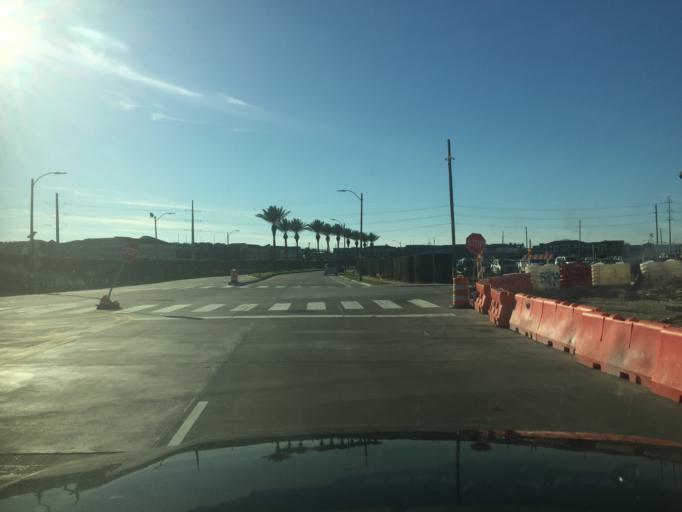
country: US
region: Louisiana
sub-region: Orleans Parish
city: New Orleans
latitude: 29.9350
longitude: -90.0639
